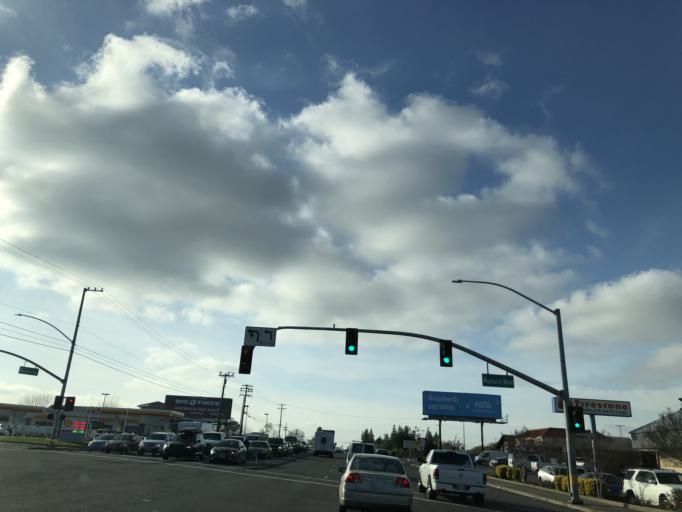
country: US
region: California
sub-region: Sacramento County
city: Foothill Farms
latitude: 38.6610
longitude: -121.3467
